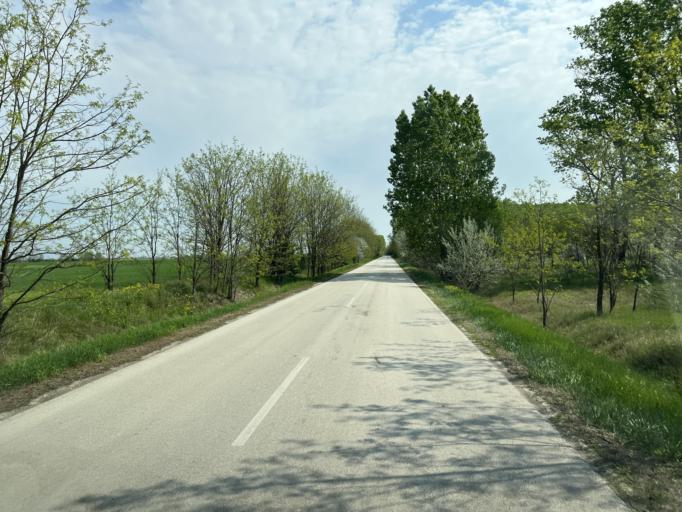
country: HU
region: Pest
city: Jaszkarajeno
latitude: 47.0709
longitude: 19.9963
